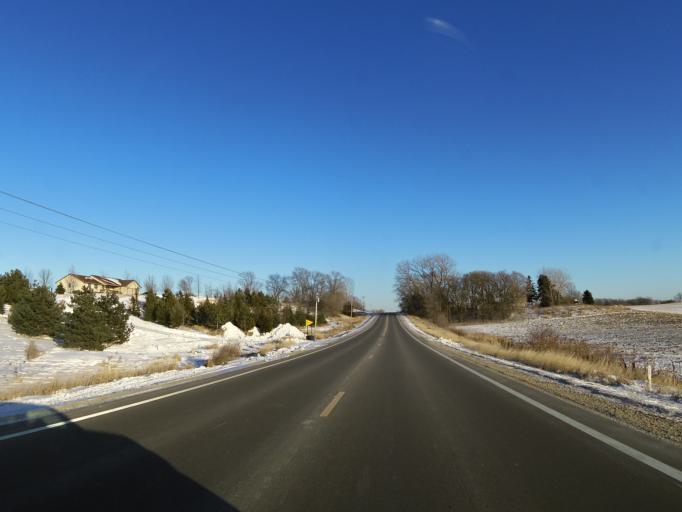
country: US
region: Minnesota
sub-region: Scott County
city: Elko New Market
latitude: 44.5439
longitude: -93.3728
